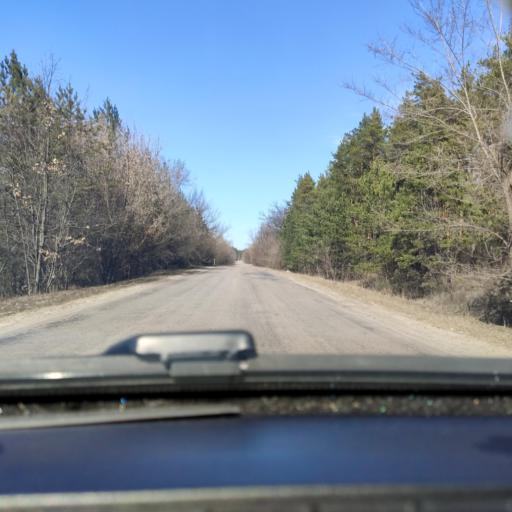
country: RU
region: Voronezj
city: Somovo
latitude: 51.7165
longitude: 39.3668
